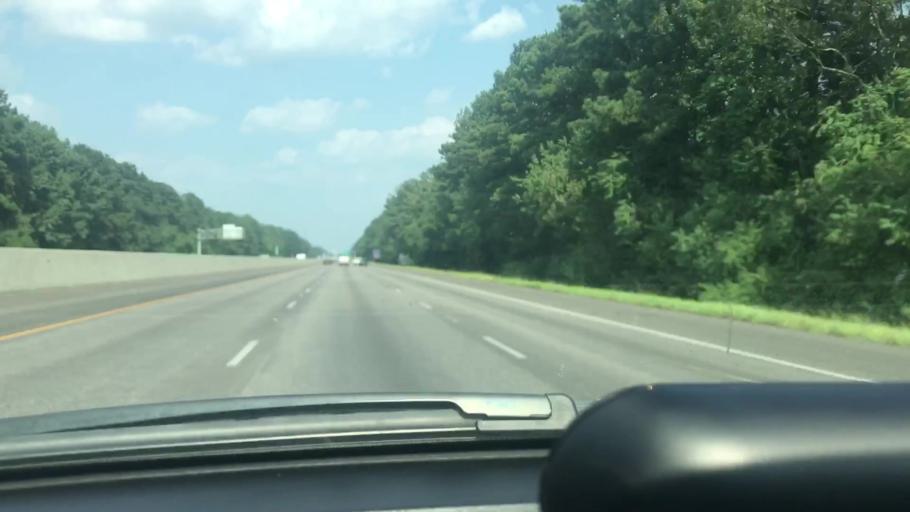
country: US
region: Louisiana
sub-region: Livingston Parish
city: Walker
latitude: 30.4683
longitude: -90.8835
